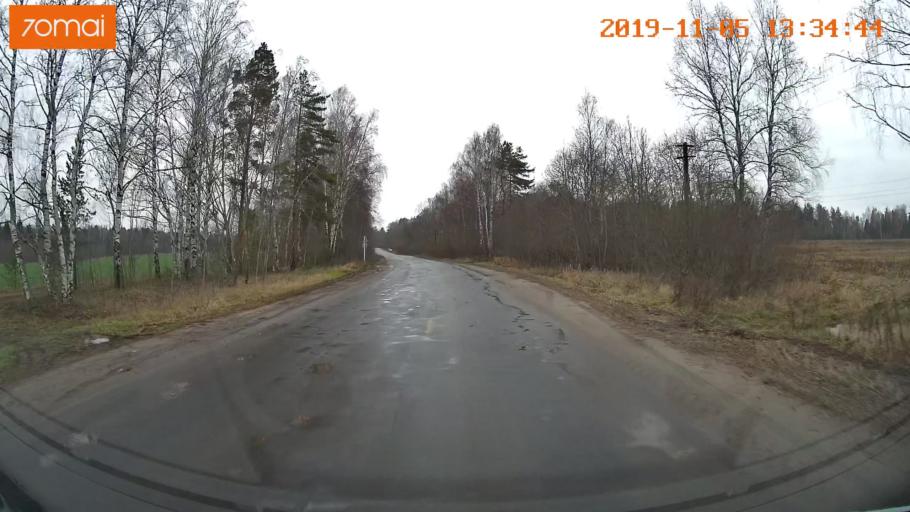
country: RU
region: Ivanovo
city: Shuya
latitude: 56.9030
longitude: 41.3898
